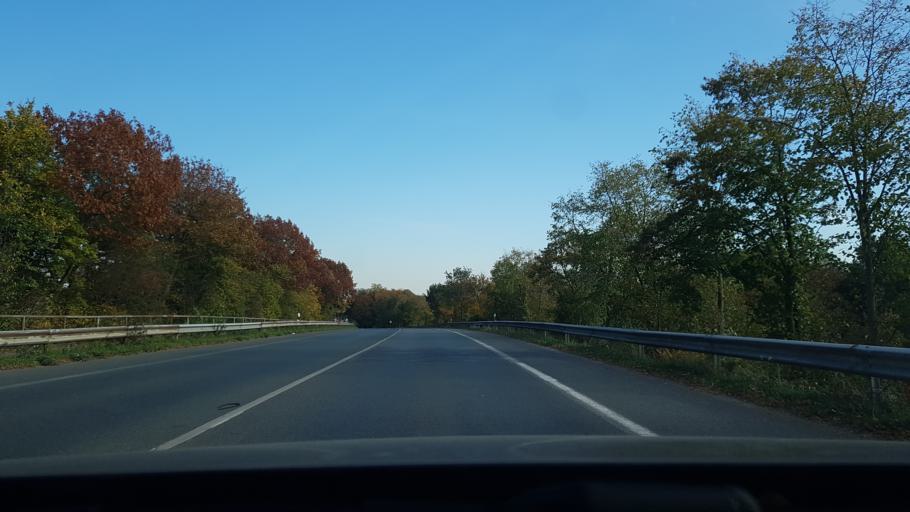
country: DE
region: North Rhine-Westphalia
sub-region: Regierungsbezirk Dusseldorf
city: Moers
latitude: 51.4468
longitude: 6.5907
